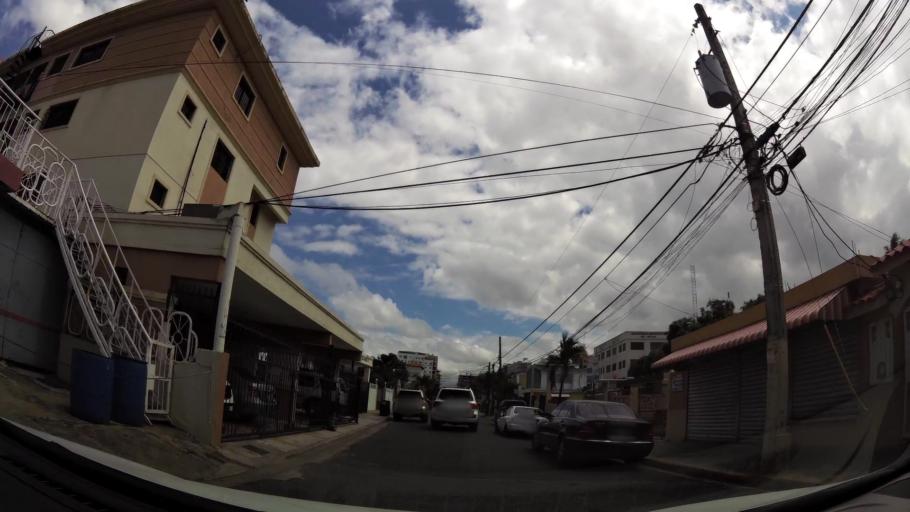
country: DO
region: Nacional
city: Bella Vista
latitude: 18.4592
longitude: -69.9499
